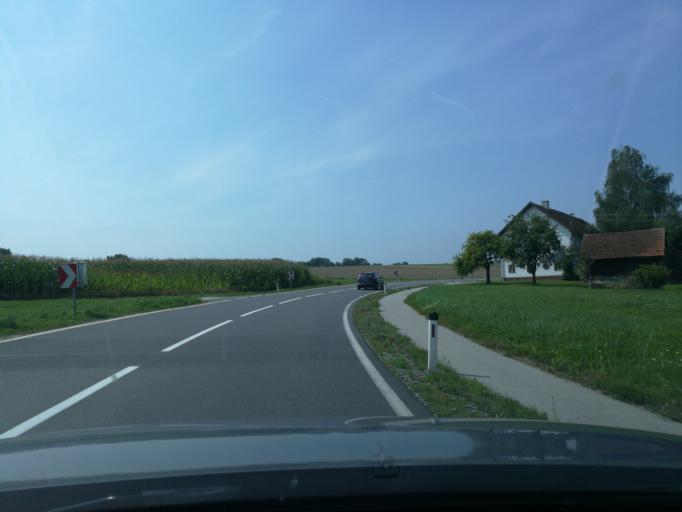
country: AT
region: Upper Austria
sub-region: Politischer Bezirk Grieskirchen
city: Grieskirchen
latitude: 48.3472
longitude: 13.7481
